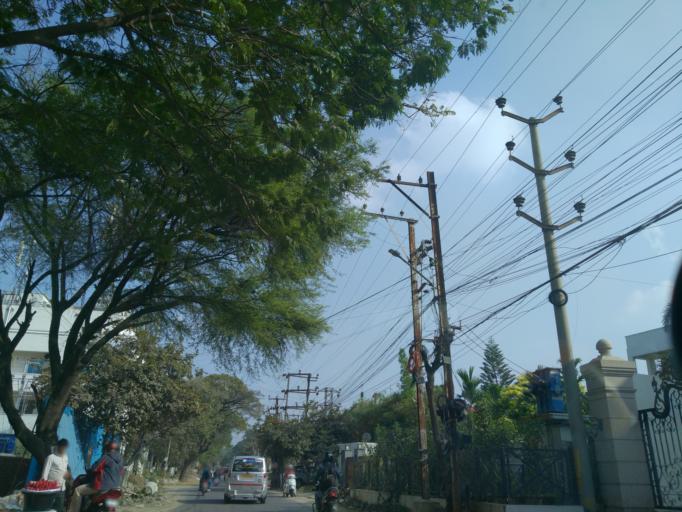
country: IN
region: Telangana
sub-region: Rangareddi
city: Kukatpalli
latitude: 17.4307
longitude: 78.4034
